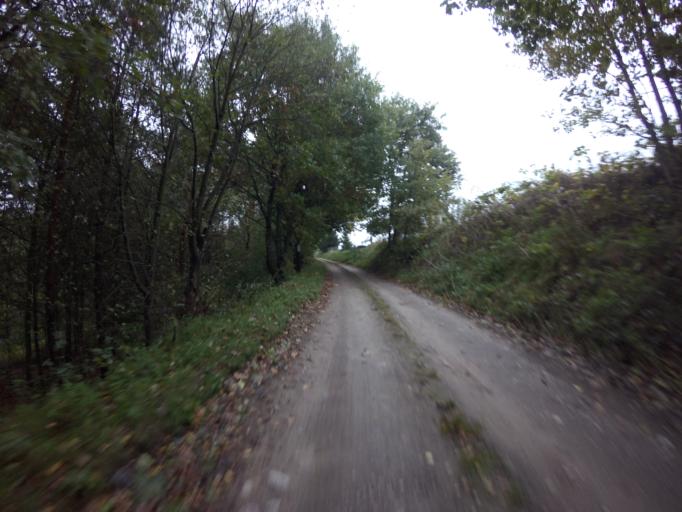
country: PL
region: Pomeranian Voivodeship
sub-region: Powiat kartuski
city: Stezyca
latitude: 54.1711
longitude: 17.9577
